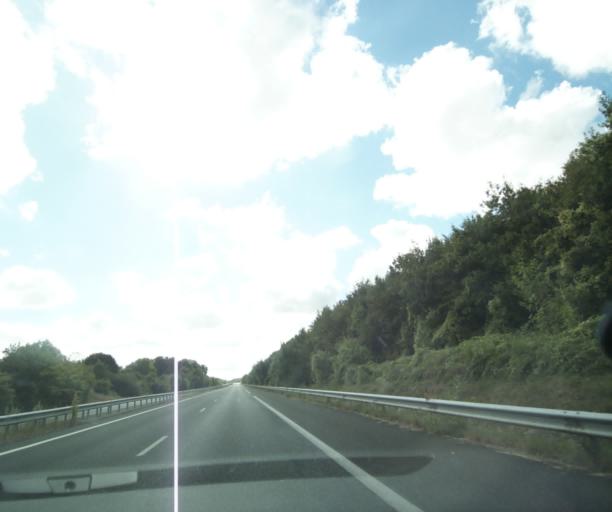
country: FR
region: Poitou-Charentes
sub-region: Departement de la Charente-Maritime
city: Cabariot
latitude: 45.9345
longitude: -0.8403
